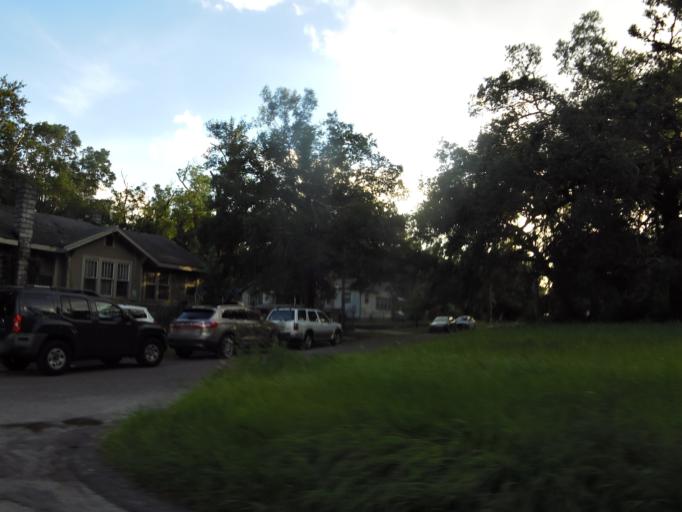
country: US
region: Florida
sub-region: Duval County
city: Jacksonville
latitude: 30.3344
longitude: -81.7023
